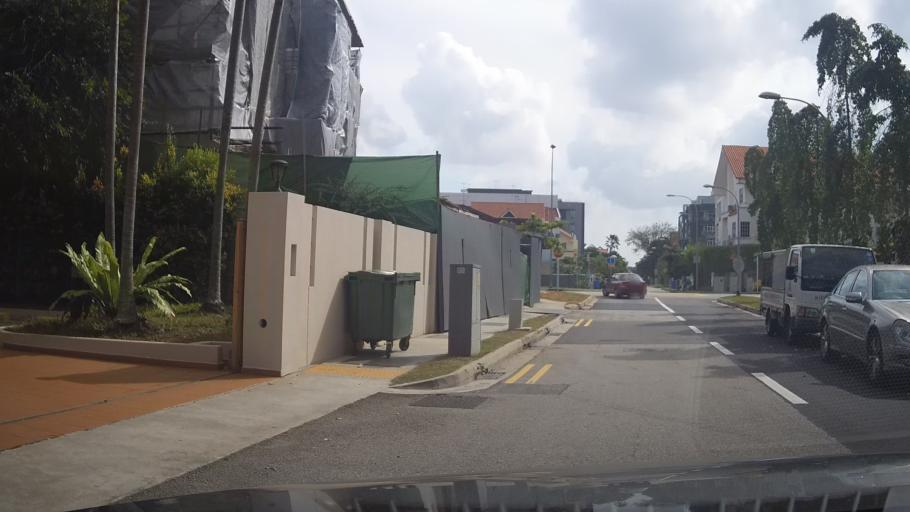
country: SG
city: Singapore
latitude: 1.3128
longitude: 103.9100
